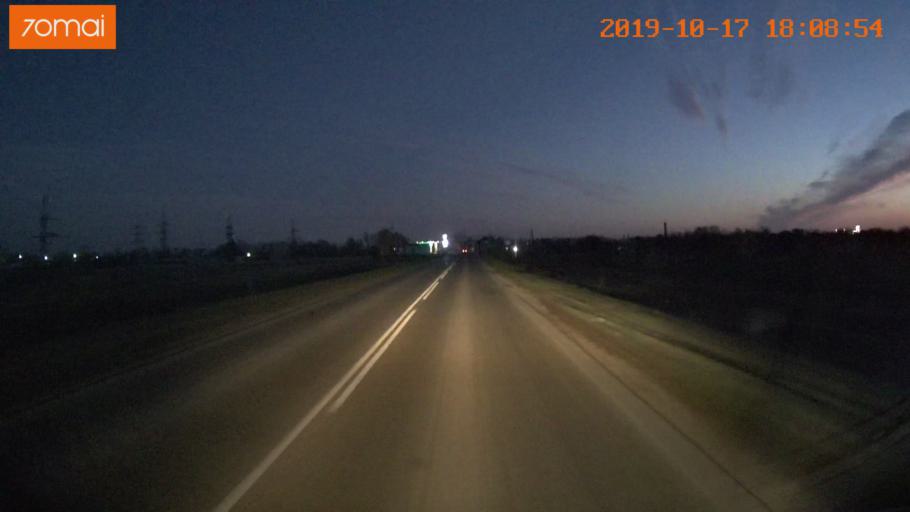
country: RU
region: Tula
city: Kurkino
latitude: 53.4284
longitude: 38.6450
